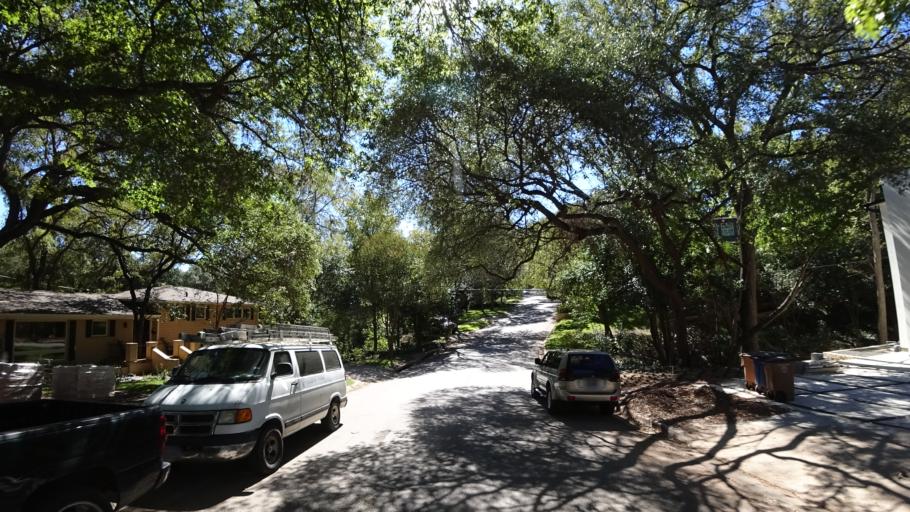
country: US
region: Texas
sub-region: Travis County
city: West Lake Hills
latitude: 30.3249
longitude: -97.7662
